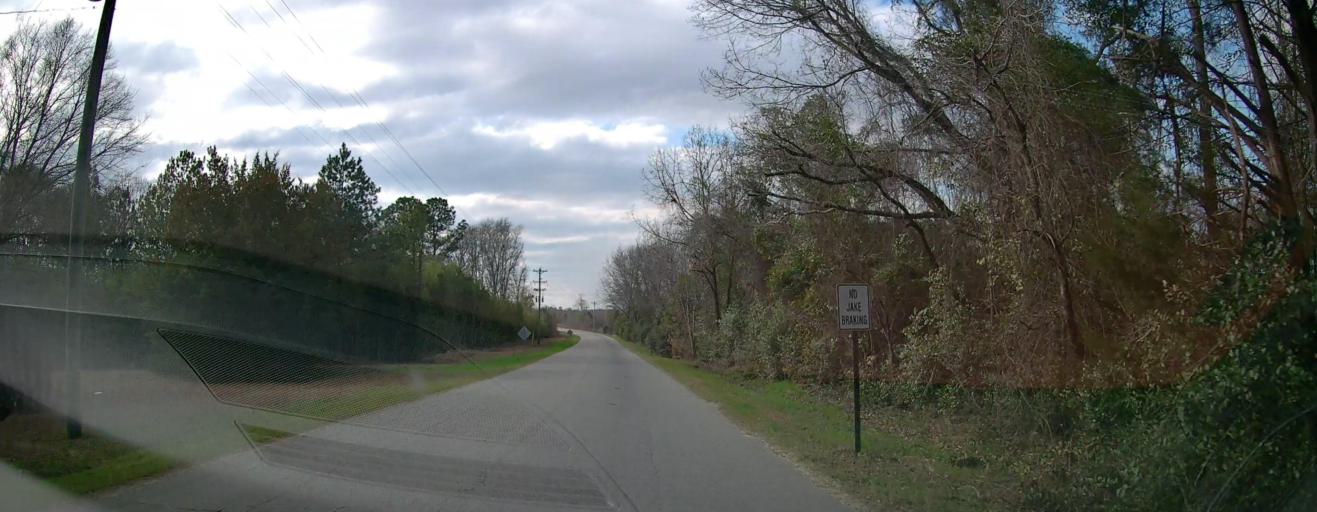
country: US
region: Georgia
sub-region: Taylor County
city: Butler
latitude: 32.4619
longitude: -84.3622
